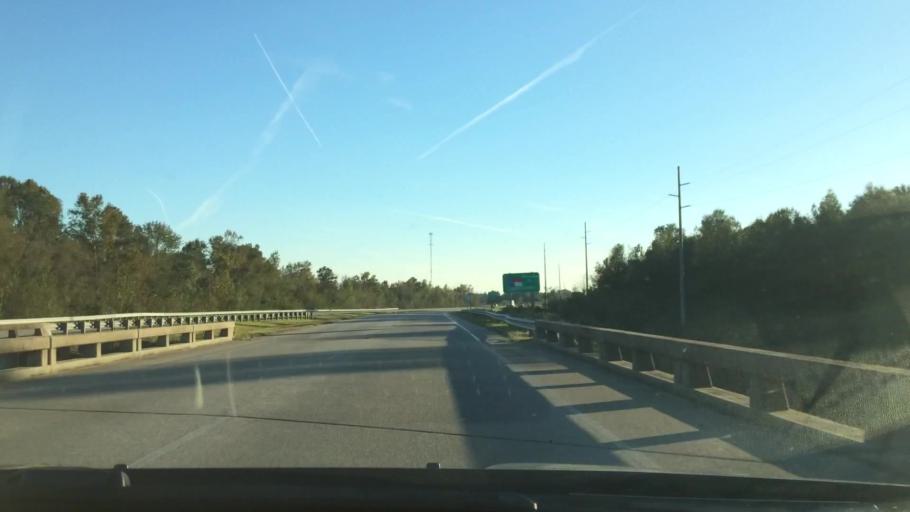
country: US
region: North Carolina
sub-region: Pitt County
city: Grifton
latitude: 35.3810
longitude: -77.4501
